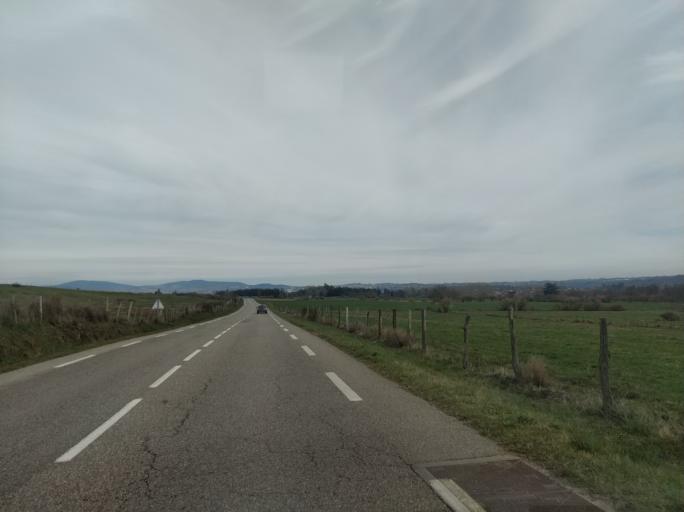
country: FR
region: Rhone-Alpes
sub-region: Departement de l'Ardeche
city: Roiffieux
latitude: 45.2004
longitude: 4.6549
